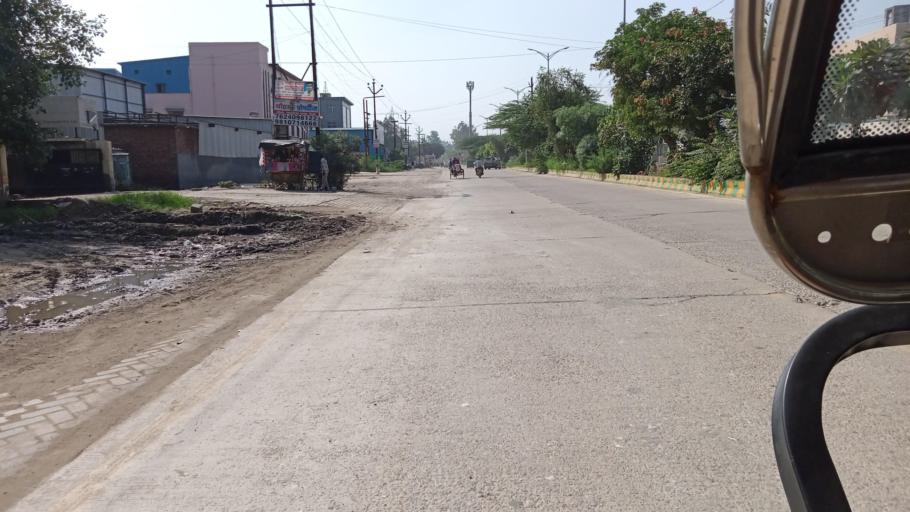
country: IN
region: Uttar Pradesh
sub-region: Ghaziabad
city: Ghaziabad
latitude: 28.6714
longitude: 77.3639
